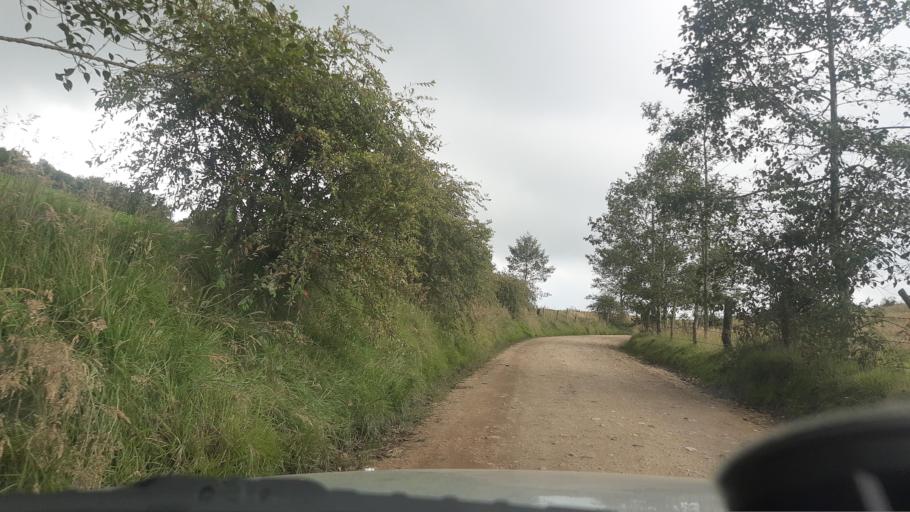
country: CO
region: Cundinamarca
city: Suesca
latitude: 5.1401
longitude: -73.7792
